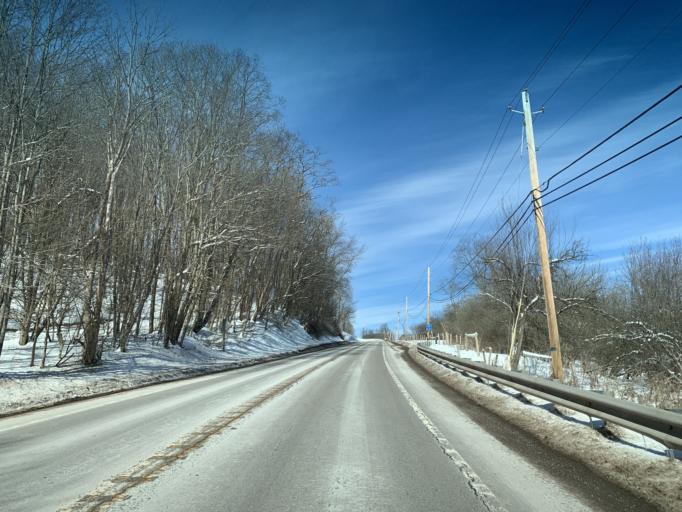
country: US
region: Pennsylvania
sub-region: Somerset County
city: Meyersdale
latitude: 39.6967
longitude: -79.1768
